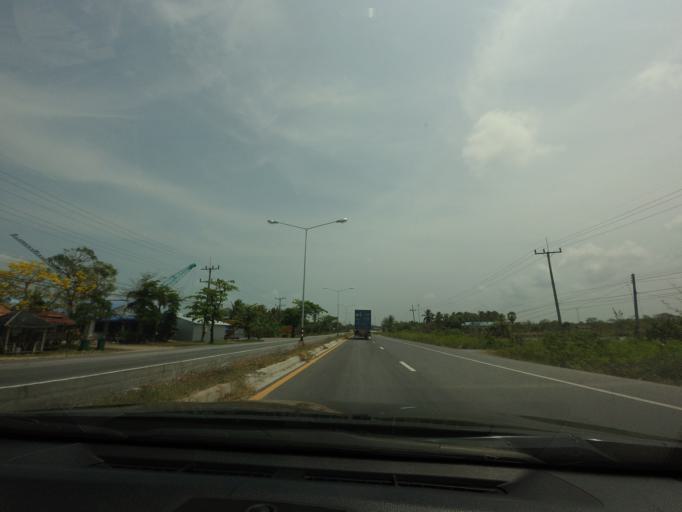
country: TH
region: Nakhon Si Thammarat
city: Hua Sai
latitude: 7.9387
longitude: 100.3336
